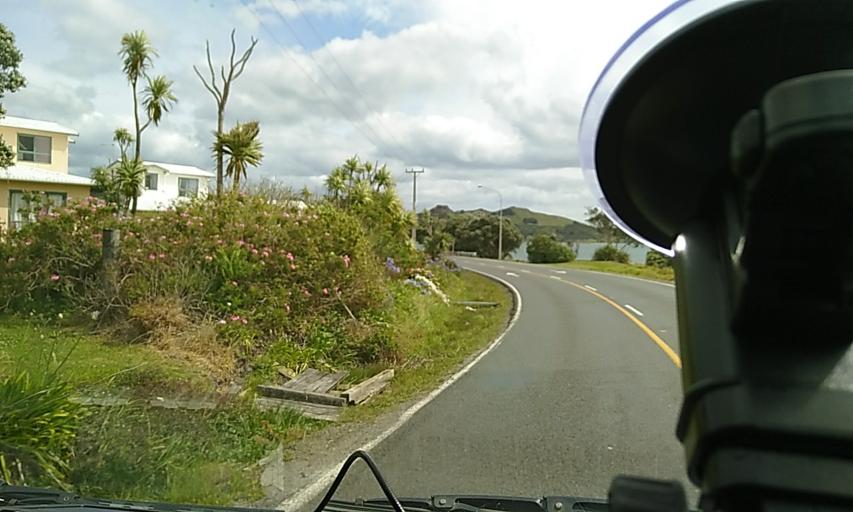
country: NZ
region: Northland
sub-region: Far North District
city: Ahipara
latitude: -35.5182
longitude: 173.3881
